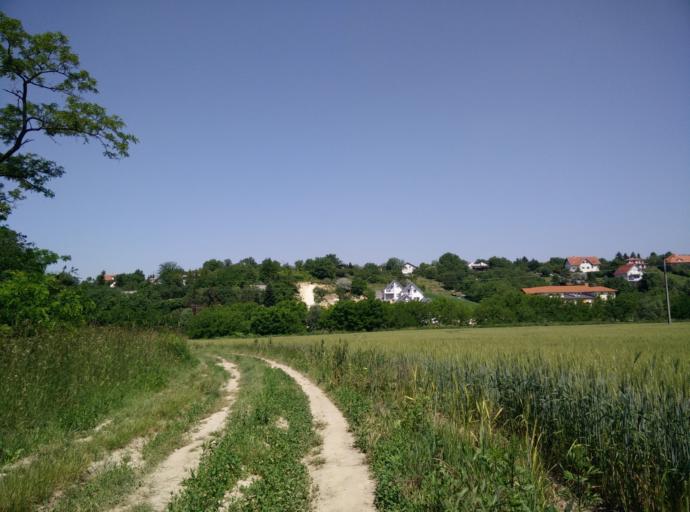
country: HU
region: Pest
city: Biatorbagy
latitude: 47.4661
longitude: 18.8296
